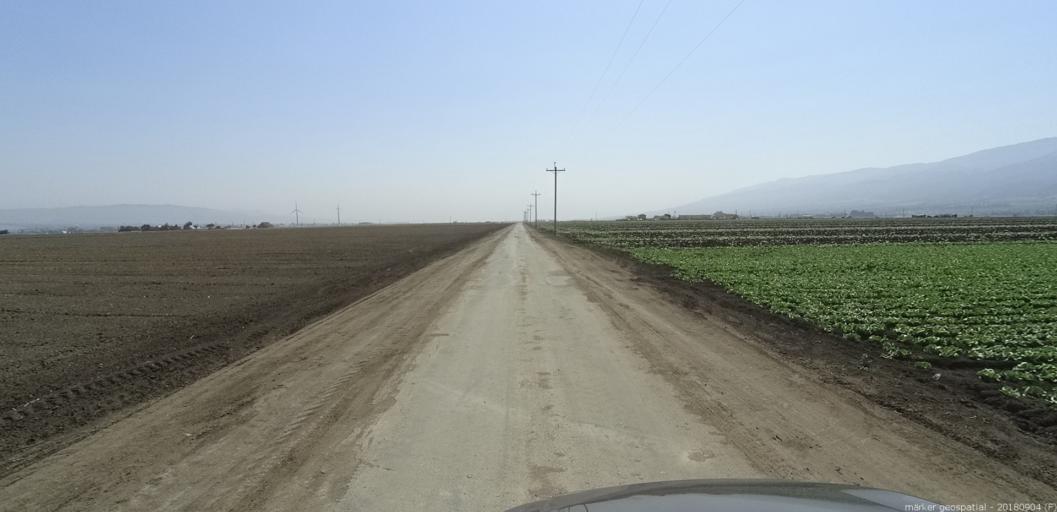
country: US
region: California
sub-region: Monterey County
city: Gonzales
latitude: 36.5138
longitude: -121.4782
